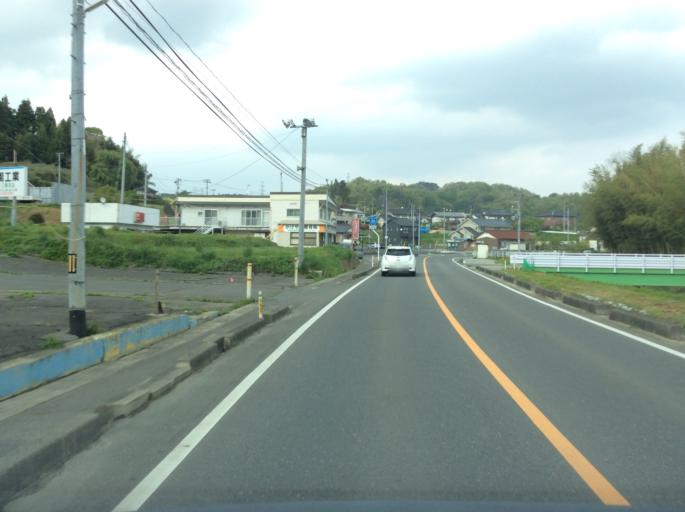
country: JP
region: Fukushima
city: Miharu
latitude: 37.4198
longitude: 140.4399
